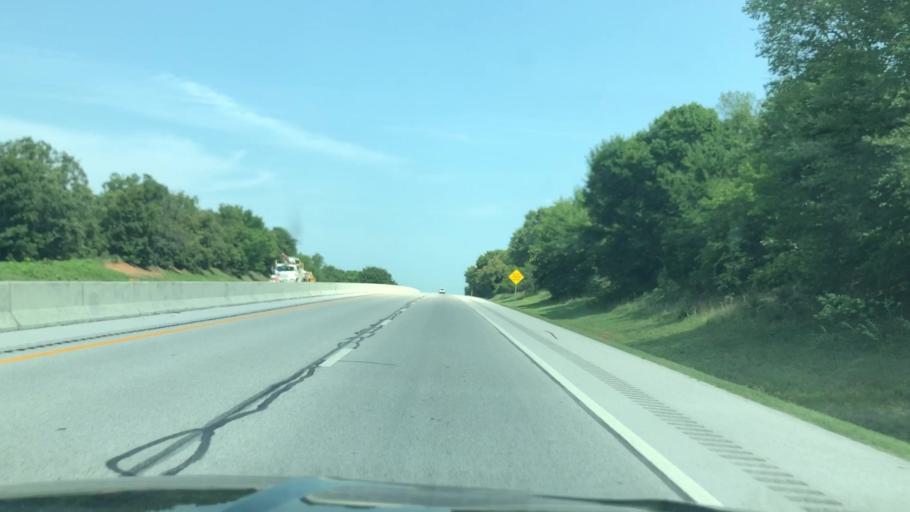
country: US
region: Oklahoma
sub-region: Rogers County
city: Justice
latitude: 36.3409
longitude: -95.4955
